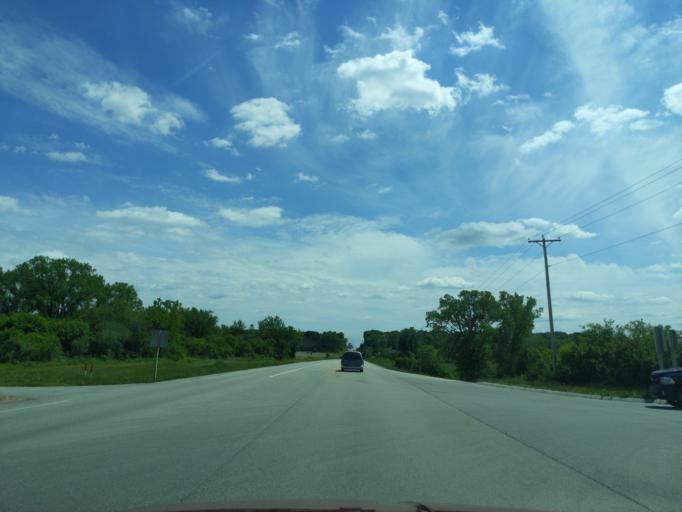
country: US
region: Wisconsin
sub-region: Columbia County
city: Poynette
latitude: 43.4047
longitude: -89.3277
